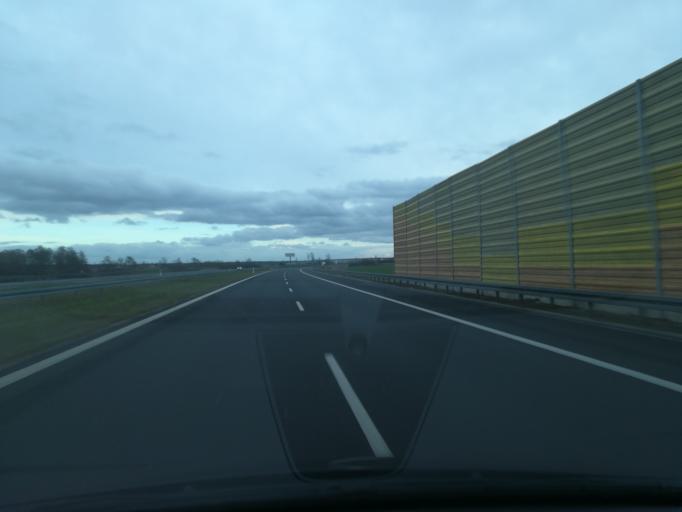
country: PL
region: Lodz Voivodeship
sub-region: Powiat kutnowski
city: Lanieta
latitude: 52.3825
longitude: 19.3018
